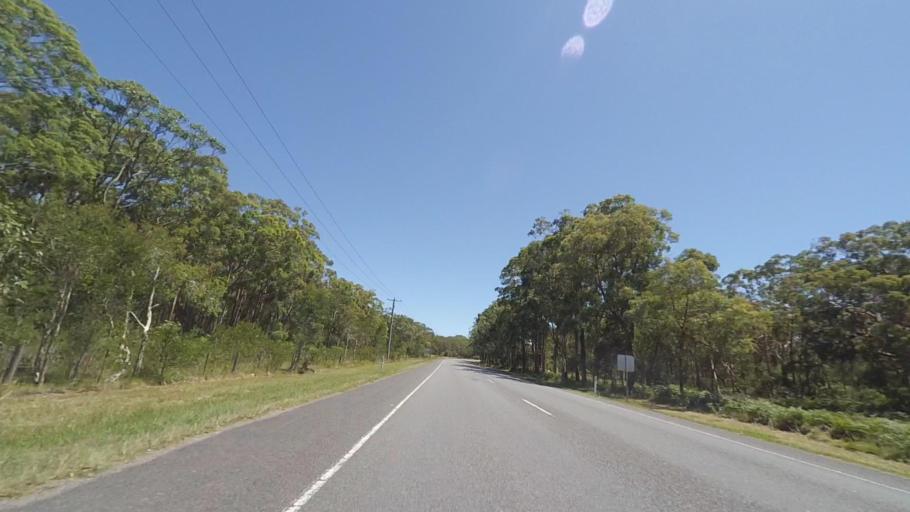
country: AU
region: New South Wales
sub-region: Port Stephens Shire
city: Medowie
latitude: -32.7782
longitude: 151.8590
